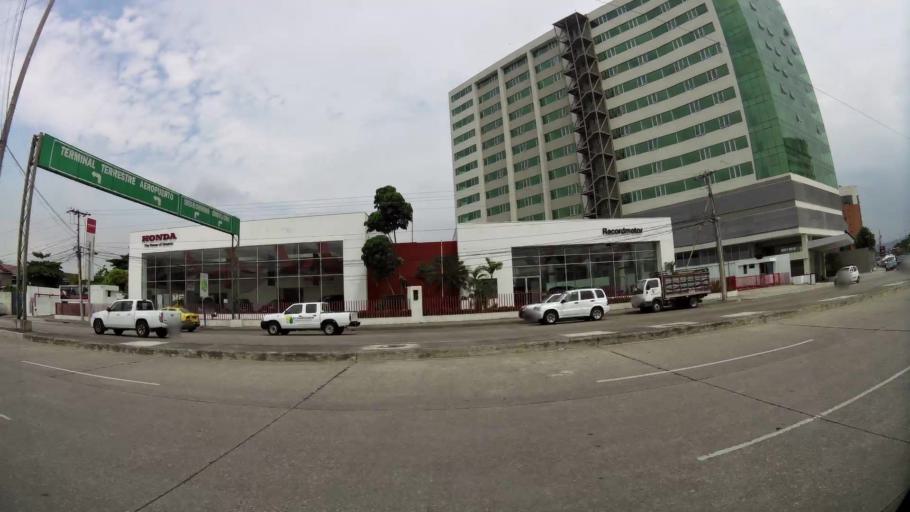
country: EC
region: Guayas
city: Eloy Alfaro
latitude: -2.1562
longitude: -79.8892
